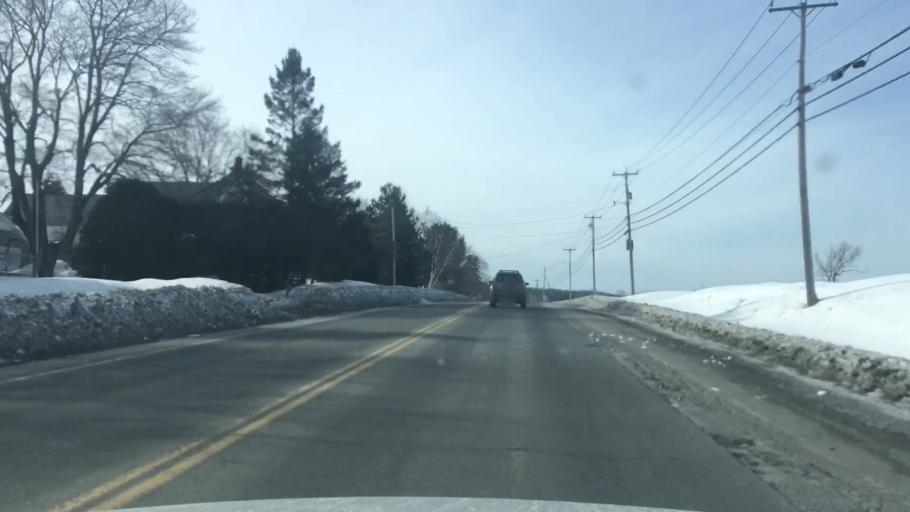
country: US
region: Maine
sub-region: Penobscot County
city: Bangor
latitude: 44.8531
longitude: -68.8110
